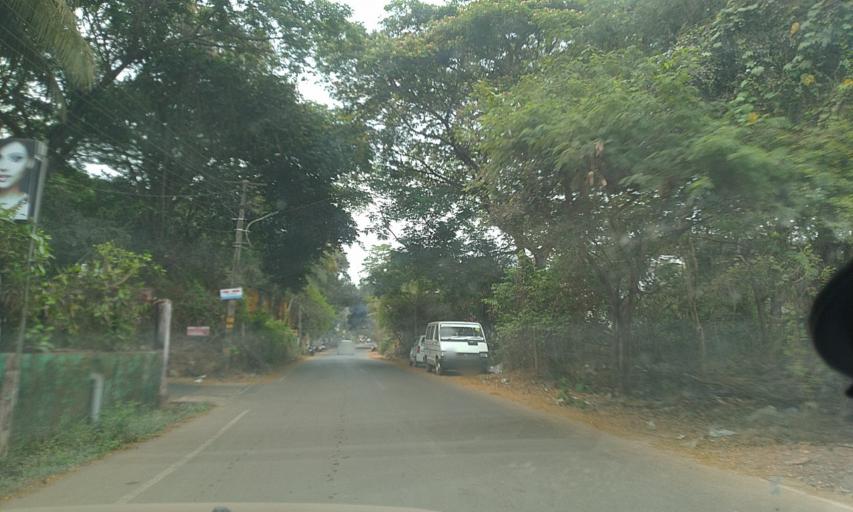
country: IN
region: Goa
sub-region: North Goa
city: Jua
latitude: 15.4976
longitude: 73.9129
